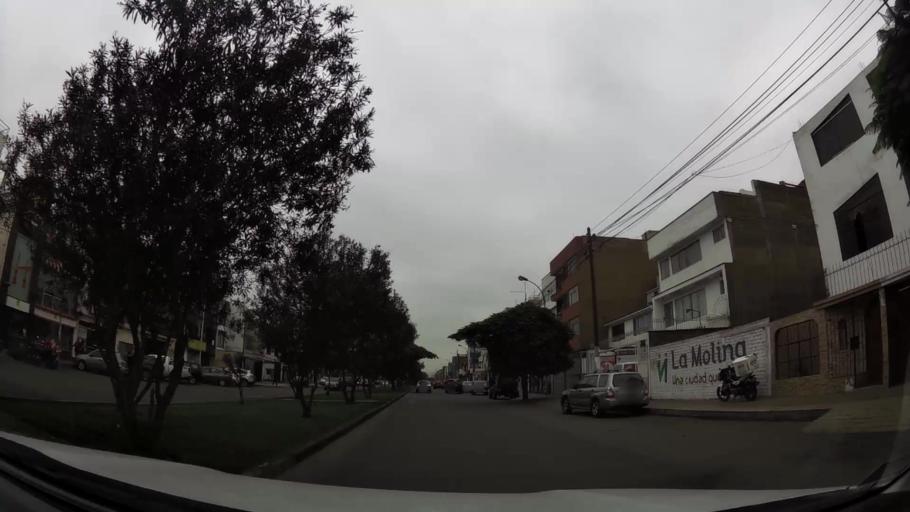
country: PE
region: Lima
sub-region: Lima
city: La Molina
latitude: -12.0710
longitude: -76.9416
